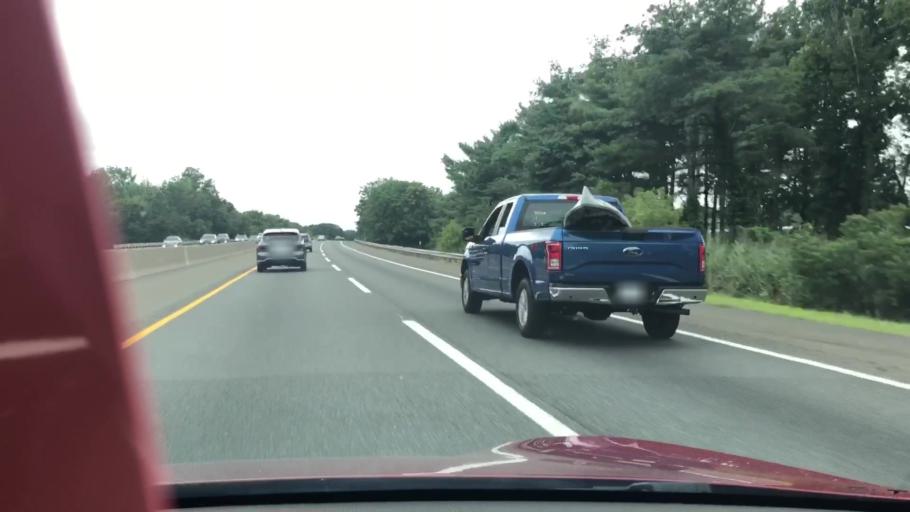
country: US
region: New Jersey
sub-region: Camden County
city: Ashland
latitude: 39.8760
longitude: -75.0109
